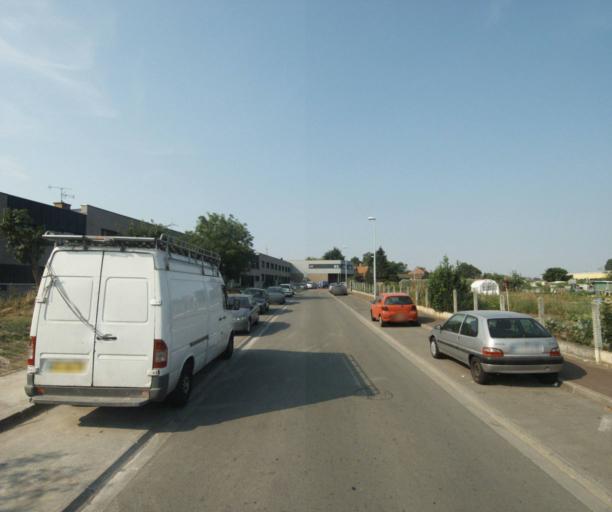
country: FR
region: Nord-Pas-de-Calais
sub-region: Departement du Nord
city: Neuville-en-Ferrain
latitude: 50.7401
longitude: 3.1458
